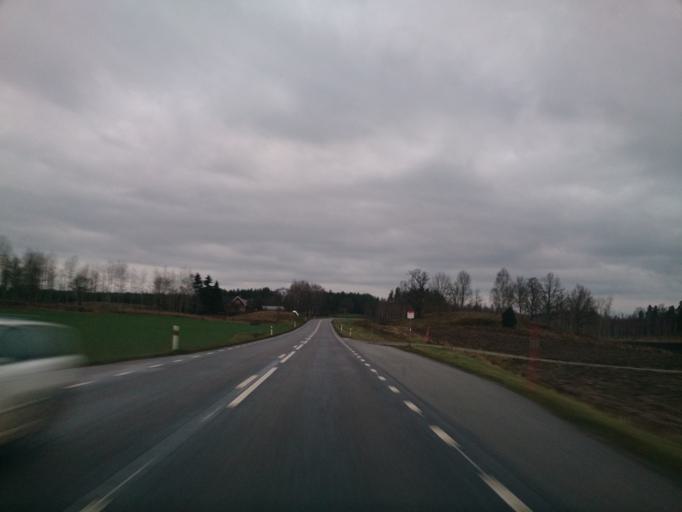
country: SE
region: OEstergoetland
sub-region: Linkopings Kommun
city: Sturefors
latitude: 58.3212
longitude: 15.8654
